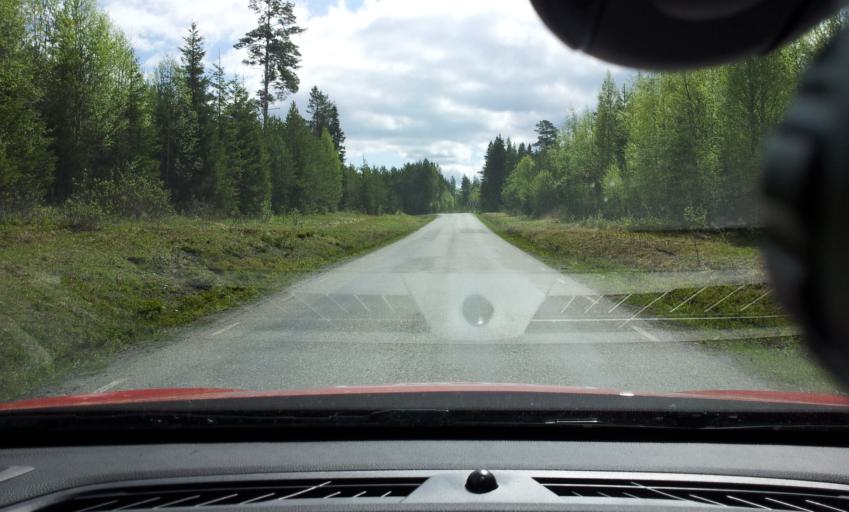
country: SE
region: Jaemtland
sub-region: OEstersunds Kommun
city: Ostersund
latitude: 63.0030
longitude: 14.6359
